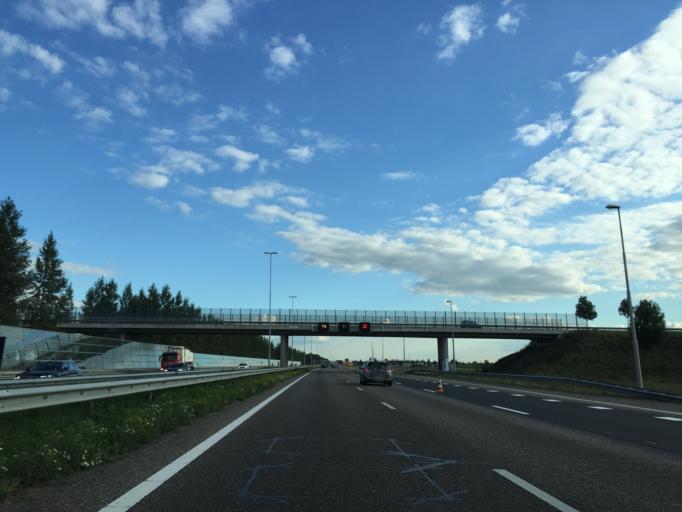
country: NL
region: North Brabant
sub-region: Gemeente Made en Drimmelen
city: Made
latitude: 51.6680
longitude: 4.6763
